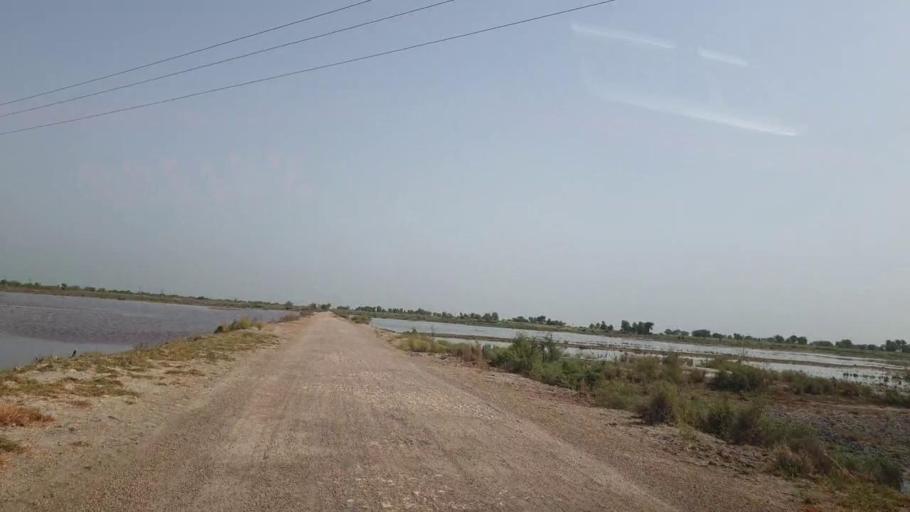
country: PK
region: Sindh
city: Sakrand
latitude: 26.3003
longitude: 68.2202
